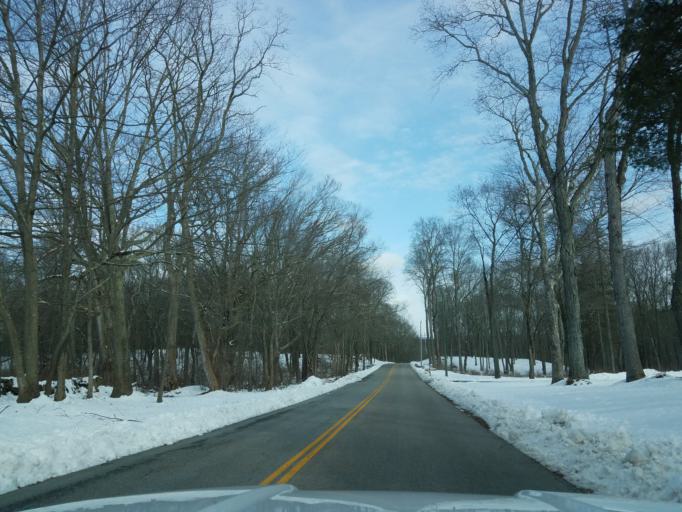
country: US
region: Connecticut
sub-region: New London County
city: Colchester
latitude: 41.5907
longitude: -72.3512
